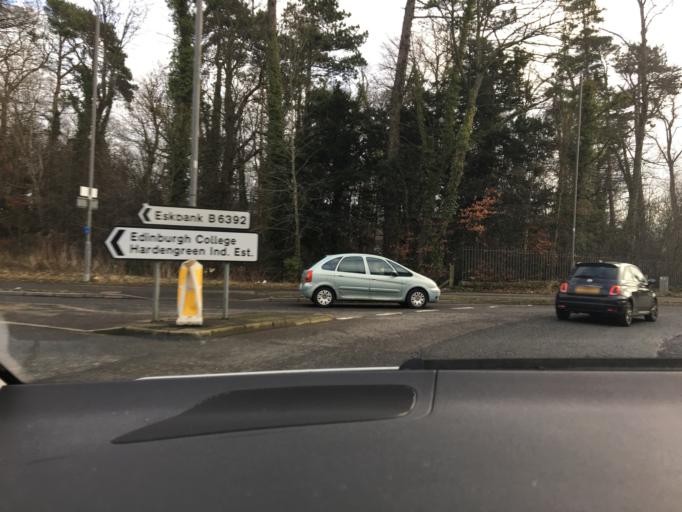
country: GB
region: Scotland
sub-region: Midlothian
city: Dalkeith
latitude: 55.8766
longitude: -3.0824
